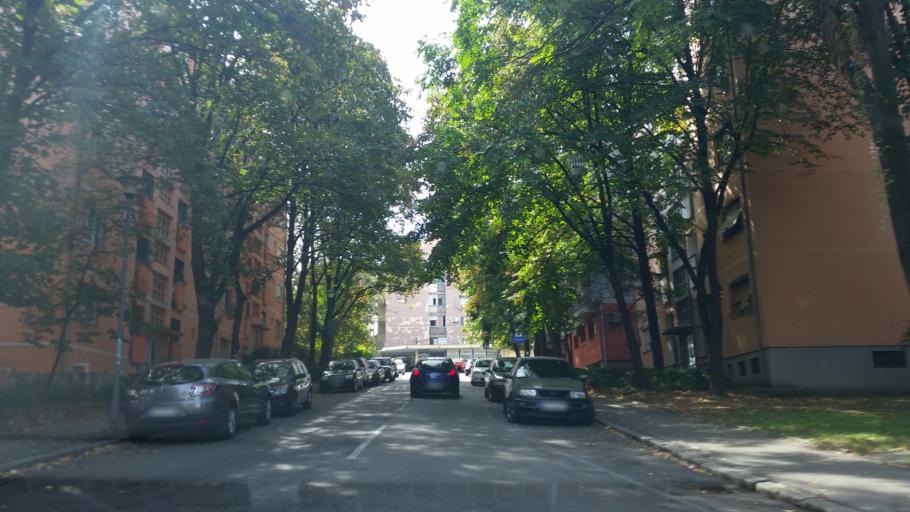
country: RS
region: Central Serbia
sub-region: Belgrade
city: Palilula
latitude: 44.8104
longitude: 20.5167
